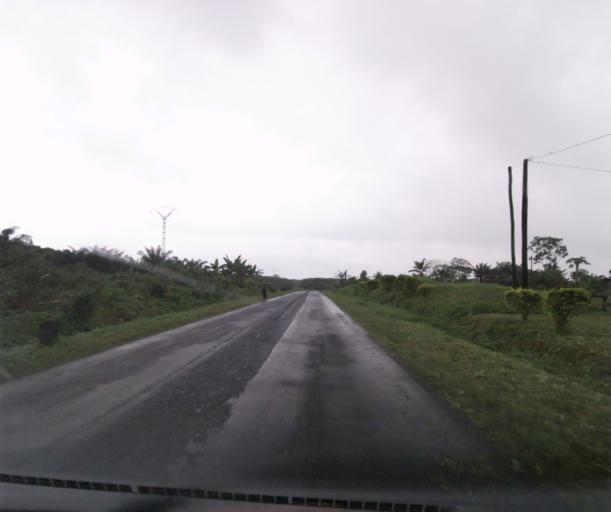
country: CM
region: South-West Province
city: Idenao
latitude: 4.1012
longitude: 8.9902
